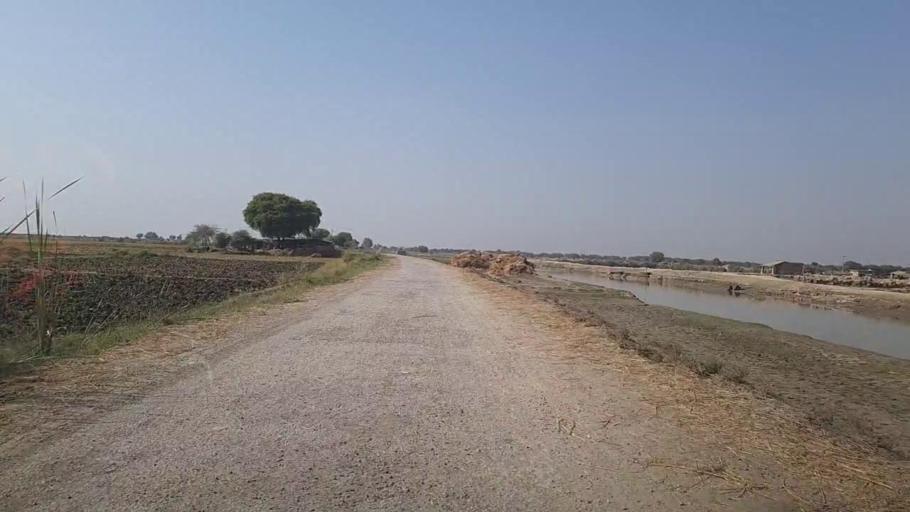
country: PK
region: Sindh
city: Kandhkot
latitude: 28.4149
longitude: 69.2367
